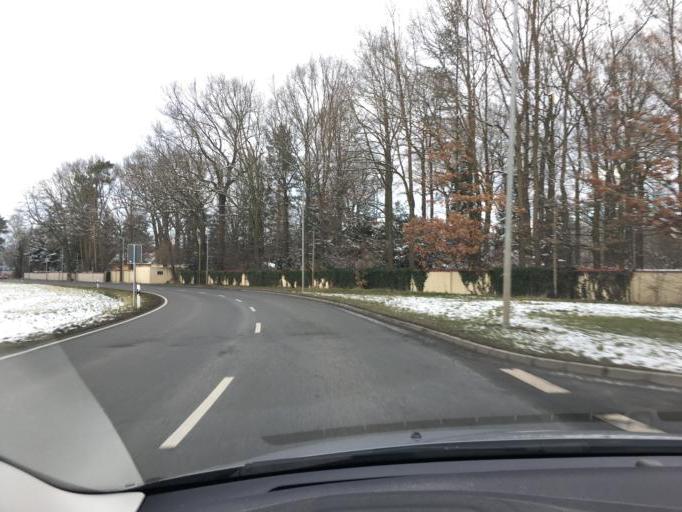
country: DE
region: Saxony
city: Brandis
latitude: 51.3084
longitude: 12.6004
